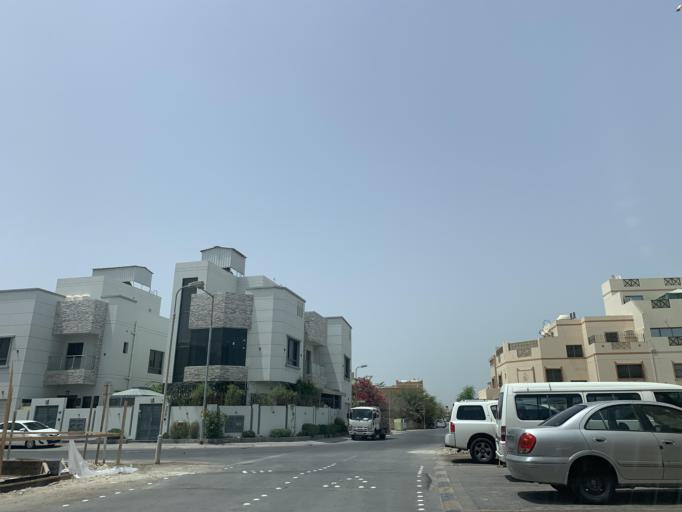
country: BH
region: Northern
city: Sitrah
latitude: 26.1458
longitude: 50.5874
